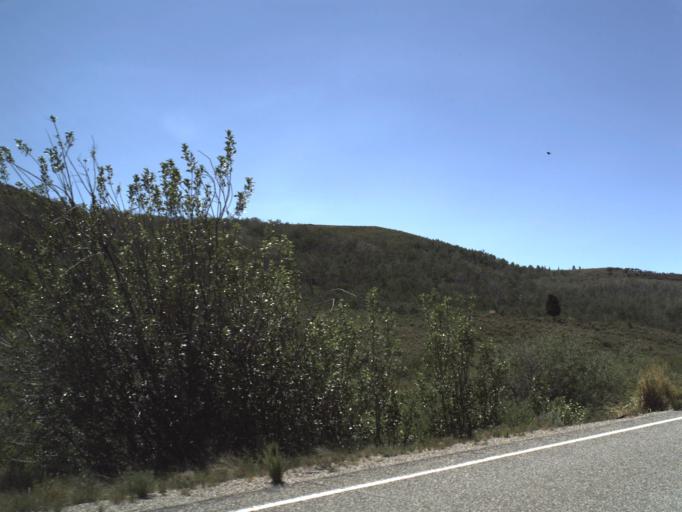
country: US
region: Utah
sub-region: Rich County
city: Randolph
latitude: 41.4778
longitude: -111.3622
